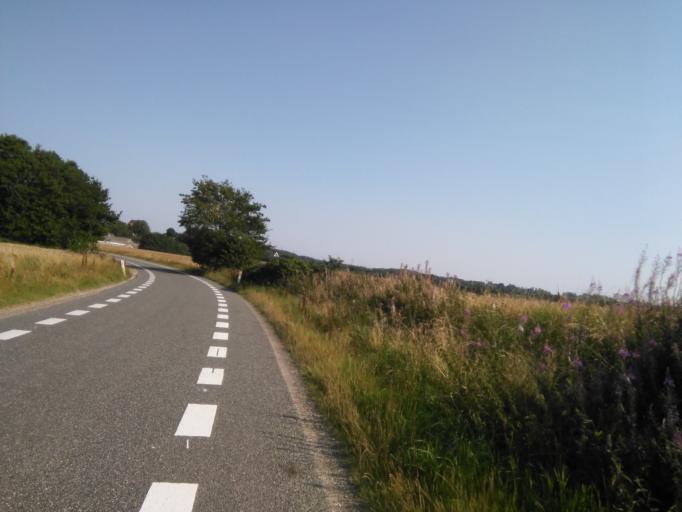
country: DK
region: Central Jutland
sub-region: Arhus Kommune
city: Framlev
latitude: 56.1346
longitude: 10.0025
